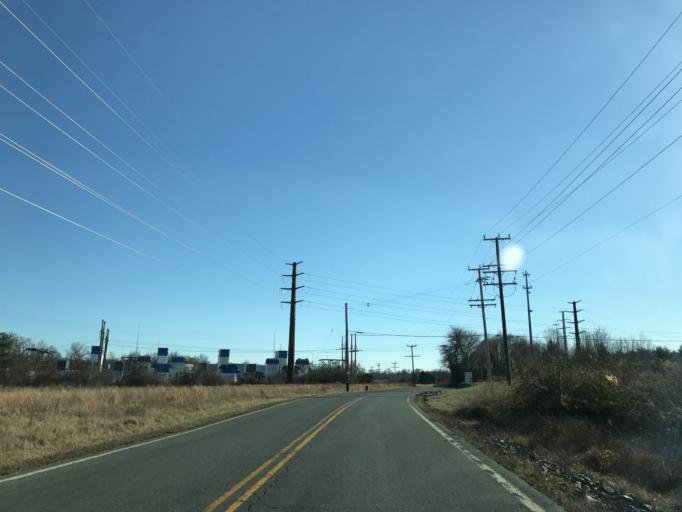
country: US
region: Maryland
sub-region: Harford County
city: Perryman
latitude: 39.4435
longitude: -76.2150
